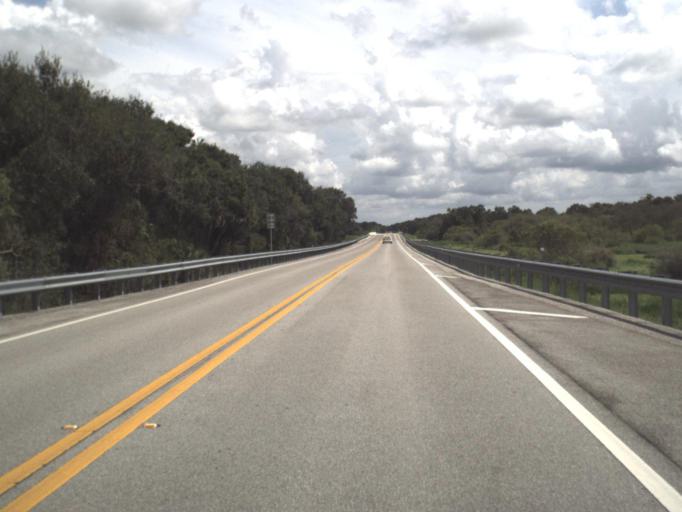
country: US
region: Florida
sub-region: Sarasota County
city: Lake Sarasota
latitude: 27.2376
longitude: -82.3148
